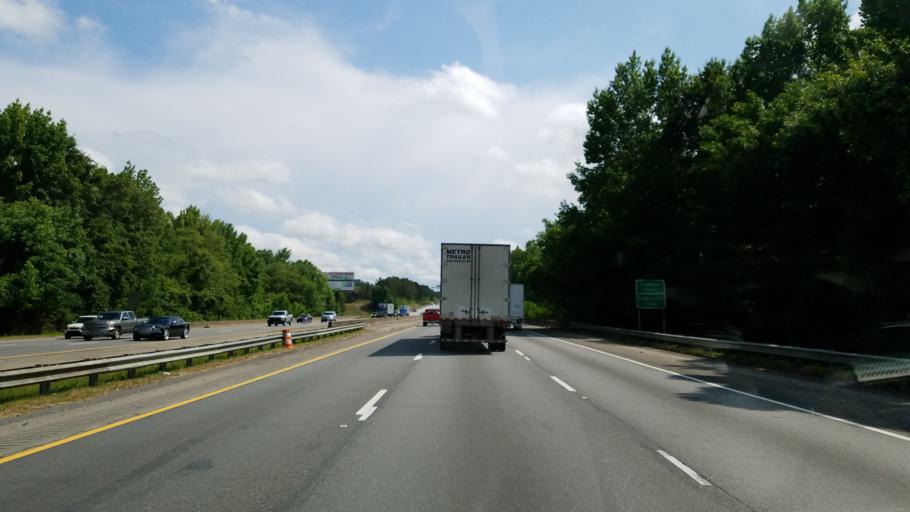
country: US
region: Georgia
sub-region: Peach County
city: Byron
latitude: 32.6960
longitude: -83.7371
